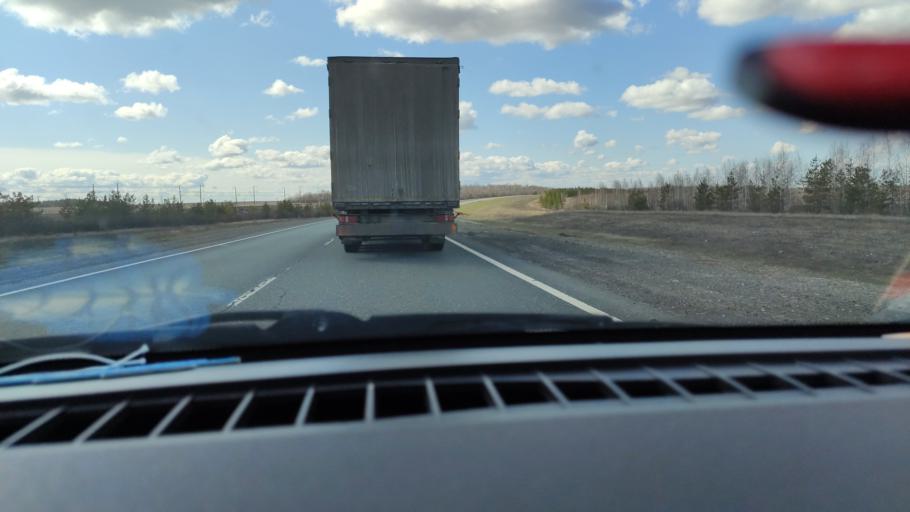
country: RU
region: Samara
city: Syzran'
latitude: 52.8736
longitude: 48.2877
